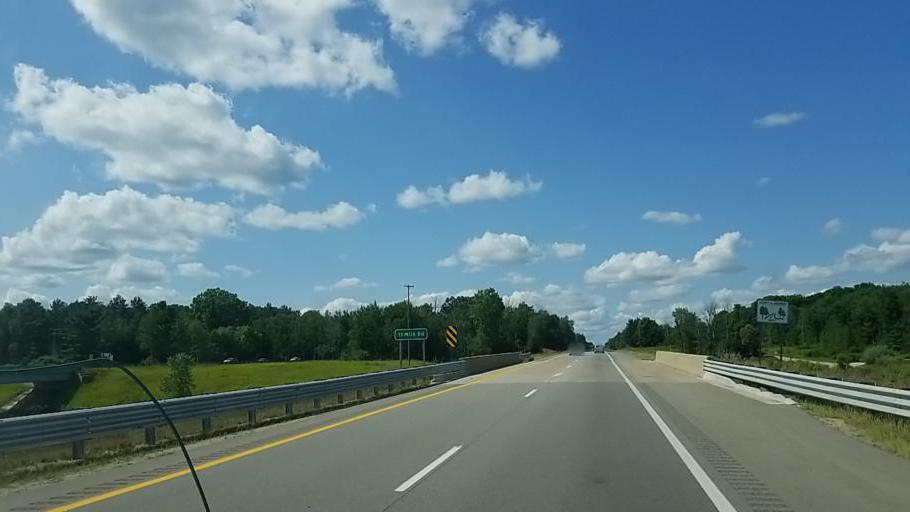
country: US
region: Michigan
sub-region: Mecosta County
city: Big Rapids
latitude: 43.6269
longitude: -85.5012
